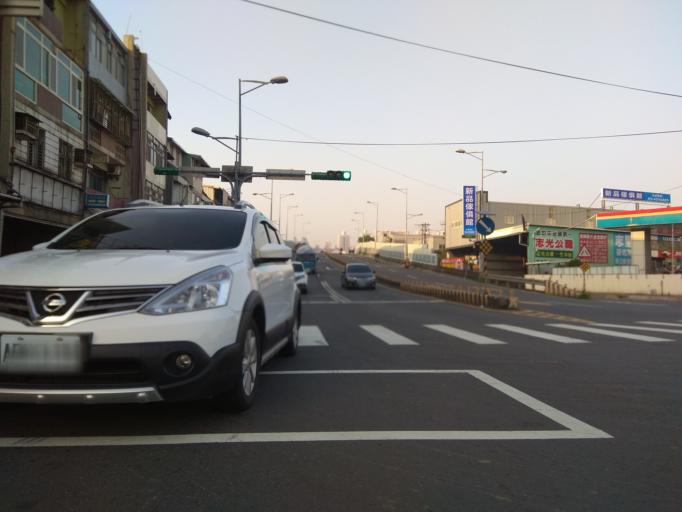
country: TW
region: Taiwan
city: Daxi
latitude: 24.9117
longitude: 121.1743
